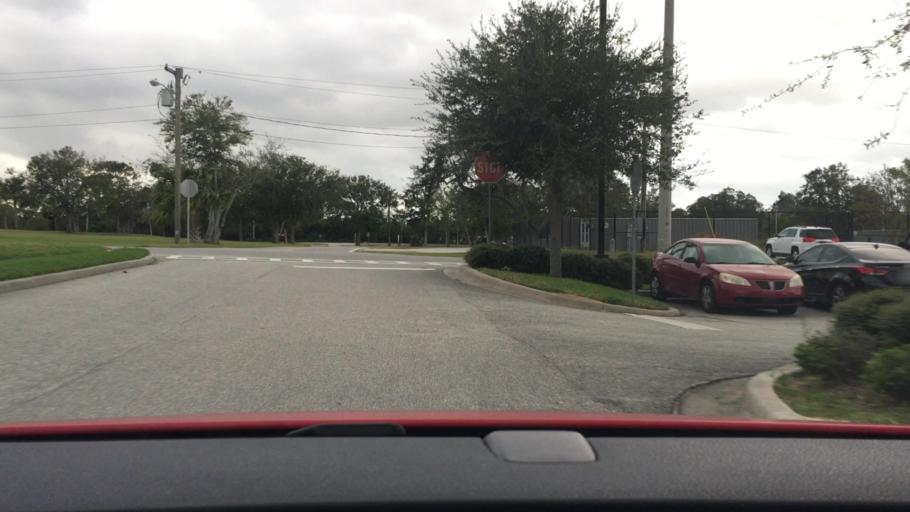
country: US
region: Florida
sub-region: Volusia County
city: Daytona Beach
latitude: 29.2045
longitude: -81.0557
